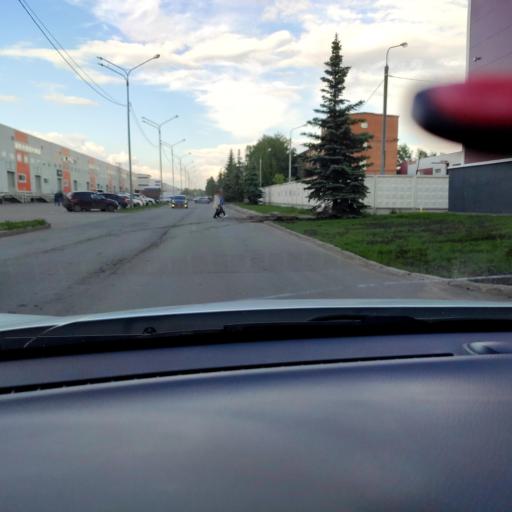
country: RU
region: Tatarstan
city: Staroye Arakchino
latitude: 55.8327
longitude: 49.0423
